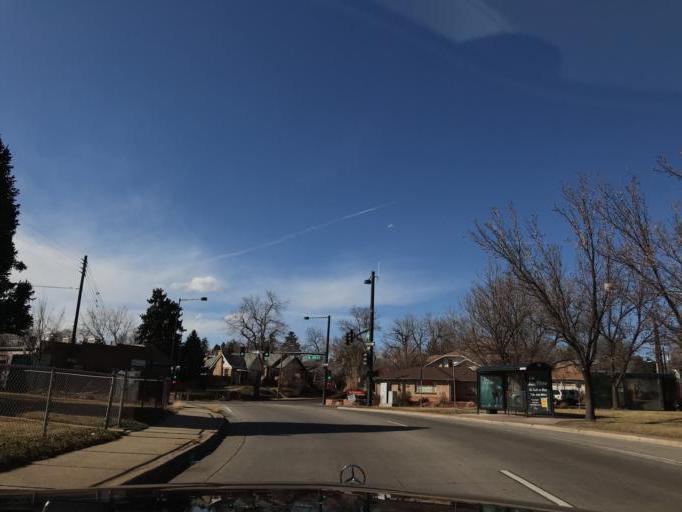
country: US
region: Colorado
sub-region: Denver County
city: Denver
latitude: 39.7250
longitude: -104.9584
